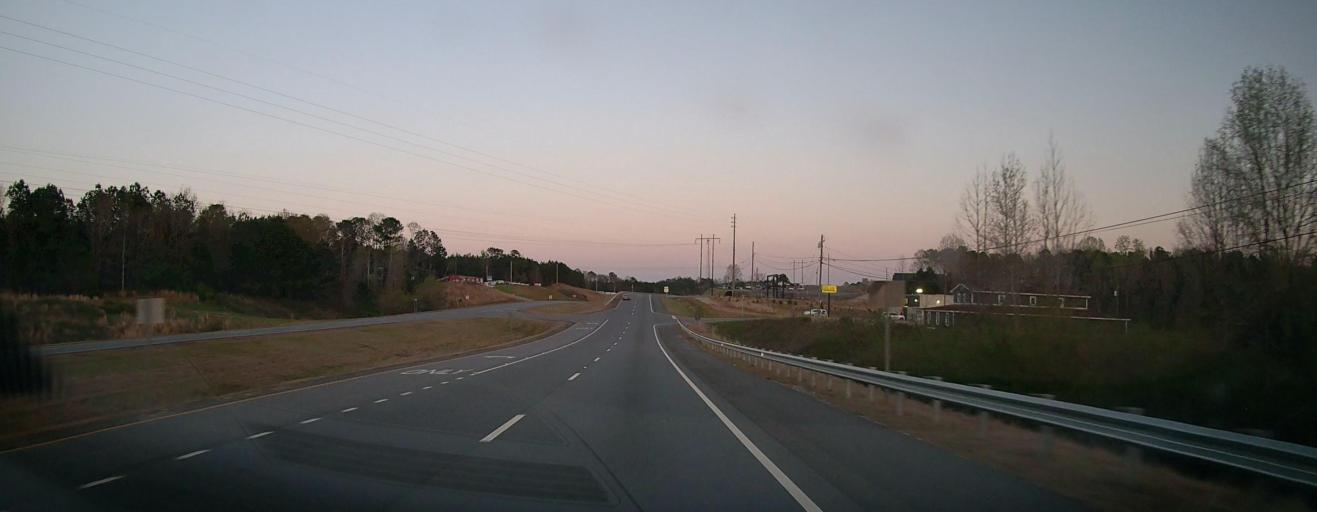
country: US
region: Alabama
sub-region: Tallapoosa County
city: Alexander City
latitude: 32.8853
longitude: -85.8639
